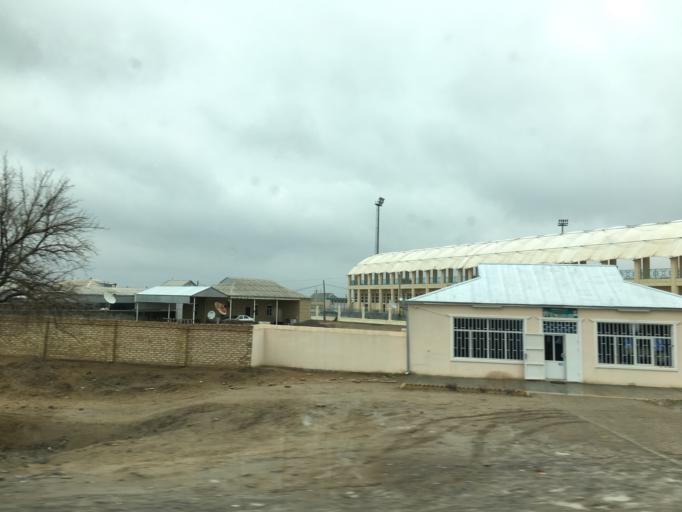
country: TM
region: Mary
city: Yoloeten
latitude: 37.2915
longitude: 62.3406
